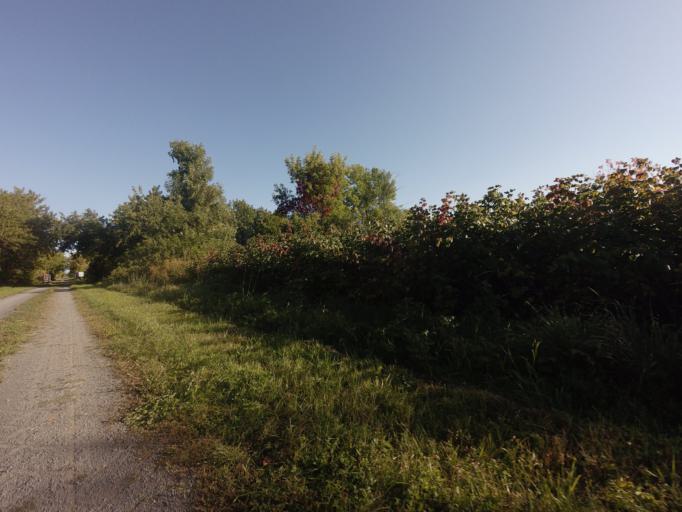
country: CA
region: Ontario
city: Hawkesbury
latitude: 45.5162
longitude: -74.5179
